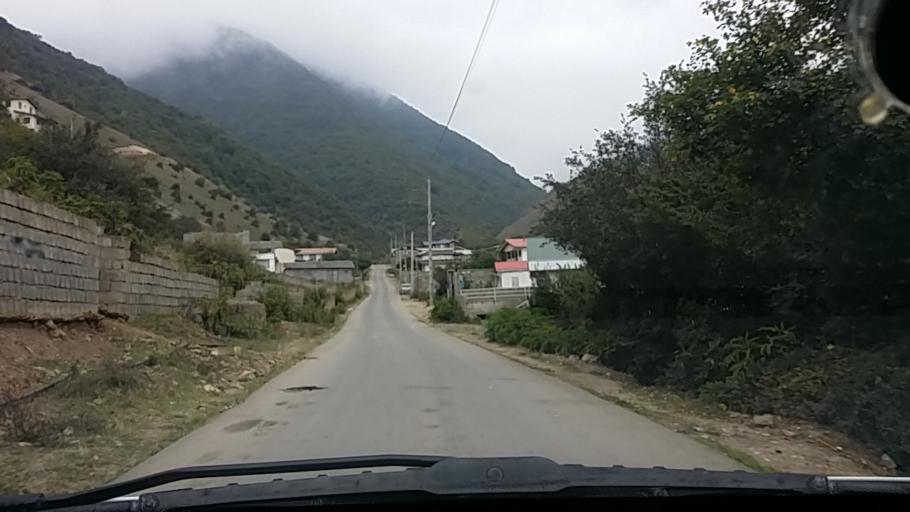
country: IR
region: Mazandaran
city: `Abbasabad
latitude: 36.4711
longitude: 51.1400
